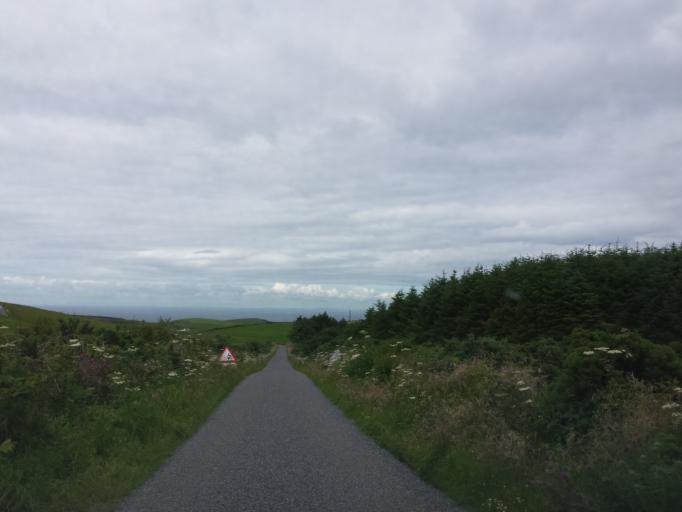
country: GB
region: Scotland
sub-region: Dumfries and Galloway
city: Stranraer
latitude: 54.8829
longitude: -5.1161
